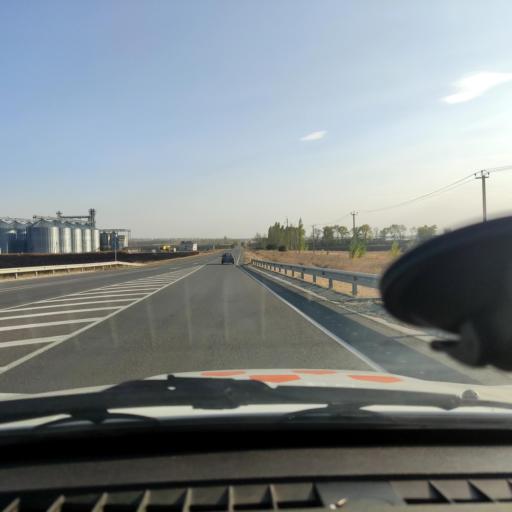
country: RU
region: Voronezj
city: Novaya Usman'
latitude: 51.5862
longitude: 39.3743
